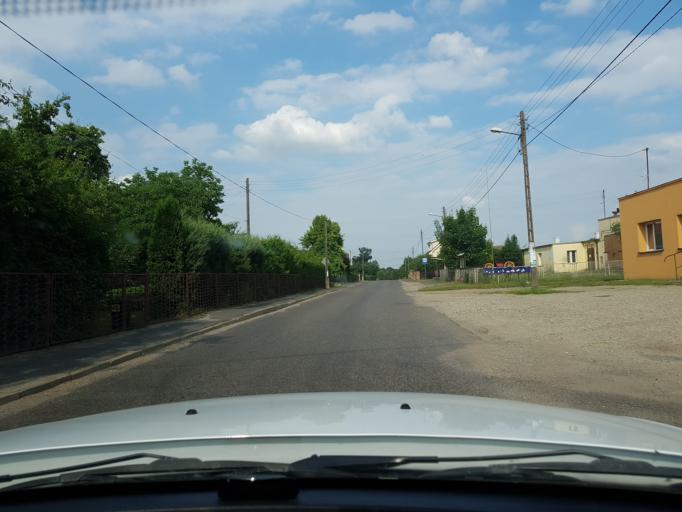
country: PL
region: West Pomeranian Voivodeship
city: Trzcinsko Zdroj
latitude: 53.0070
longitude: 14.5203
